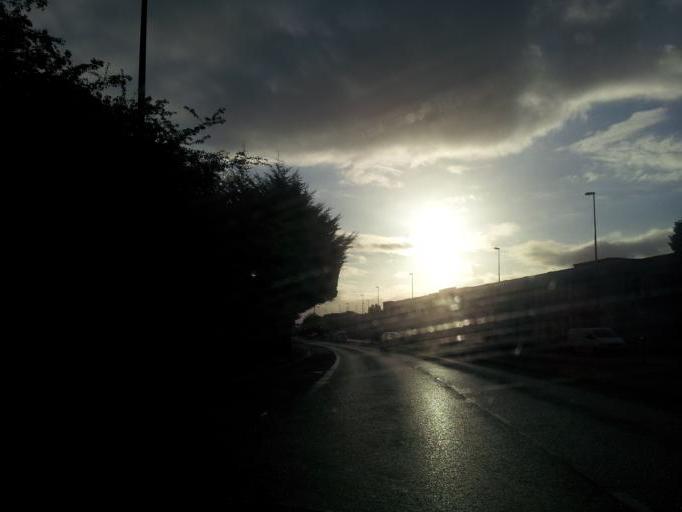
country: GB
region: England
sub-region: Trafford
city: Trafford Park
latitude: 53.4677
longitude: -2.3206
